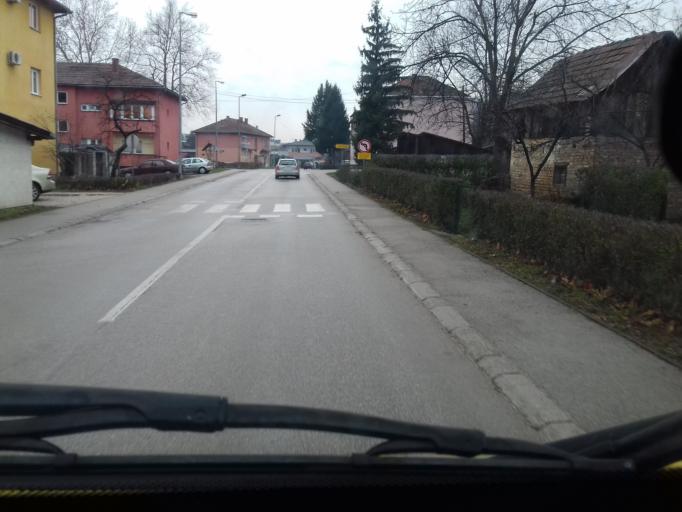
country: BA
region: Federation of Bosnia and Herzegovina
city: Maglaj
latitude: 44.5501
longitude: 18.0960
